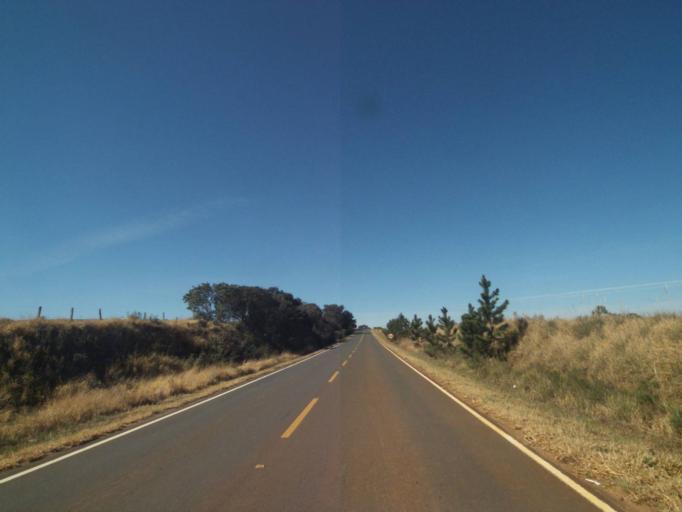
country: BR
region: Parana
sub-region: Tibagi
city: Tibagi
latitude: -24.4902
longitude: -50.4679
